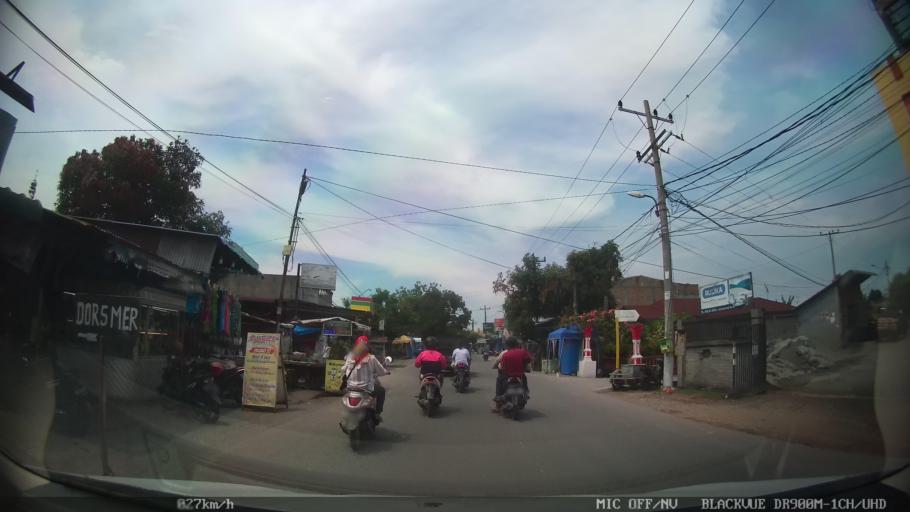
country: ID
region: North Sumatra
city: Labuhan Deli
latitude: 3.6599
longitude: 98.6776
